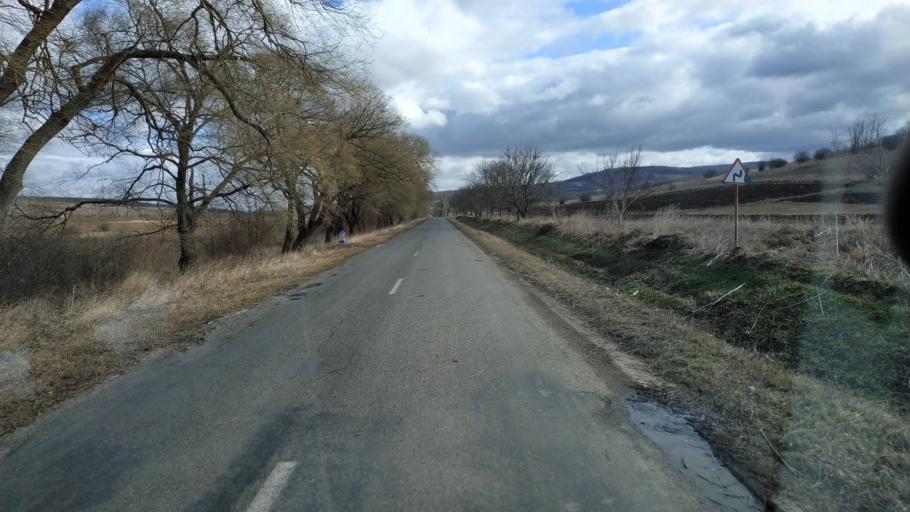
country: MD
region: Stinga Nistrului
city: Bucovat
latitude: 47.1439
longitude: 28.3577
